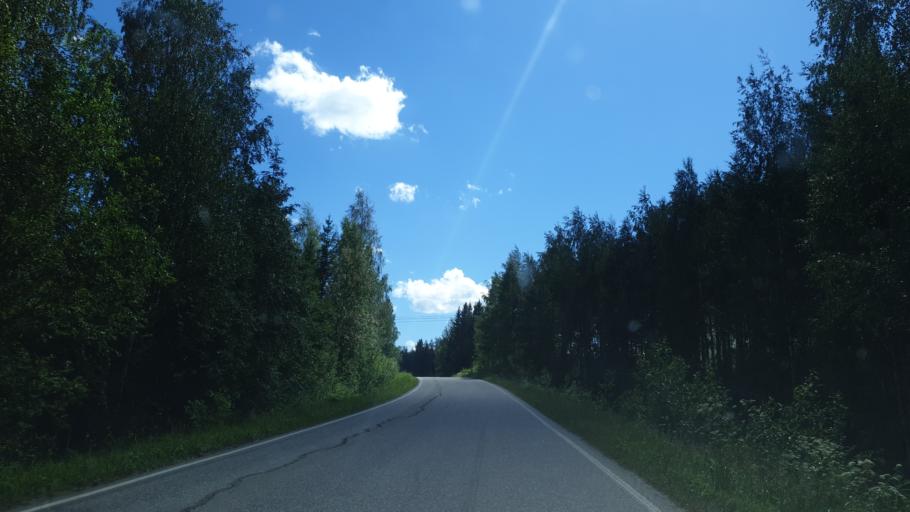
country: FI
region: Northern Savo
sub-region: Koillis-Savo
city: Kaavi
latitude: 63.0033
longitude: 28.5019
